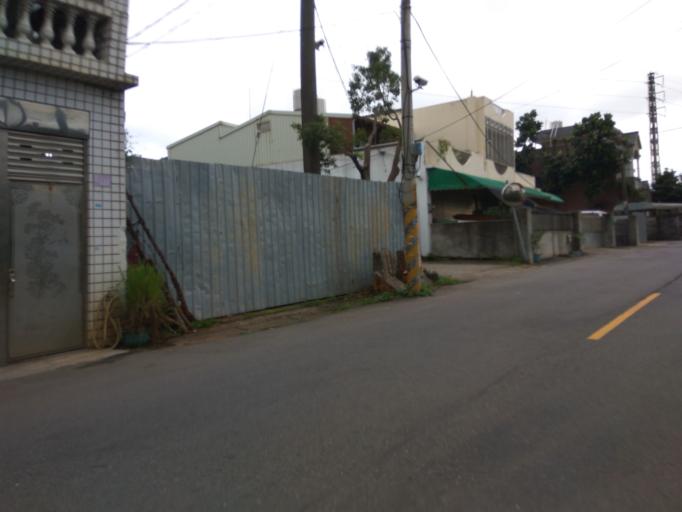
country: TW
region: Taiwan
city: Taoyuan City
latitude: 24.9850
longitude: 121.2288
